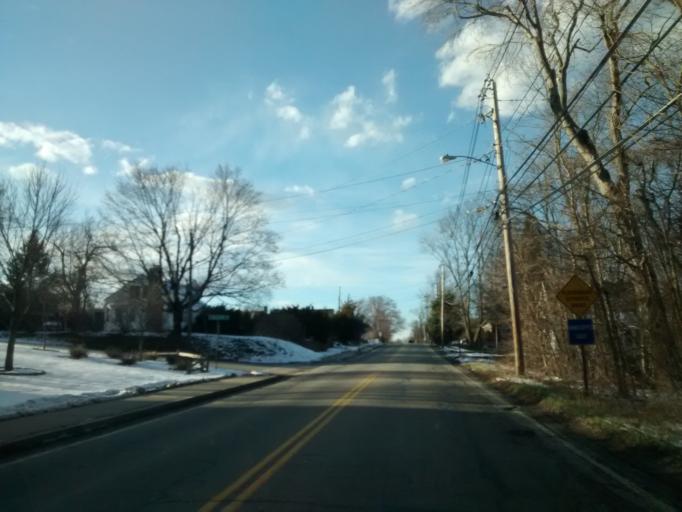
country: US
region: Massachusetts
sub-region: Middlesex County
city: Hopkinton
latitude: 42.2142
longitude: -71.5151
